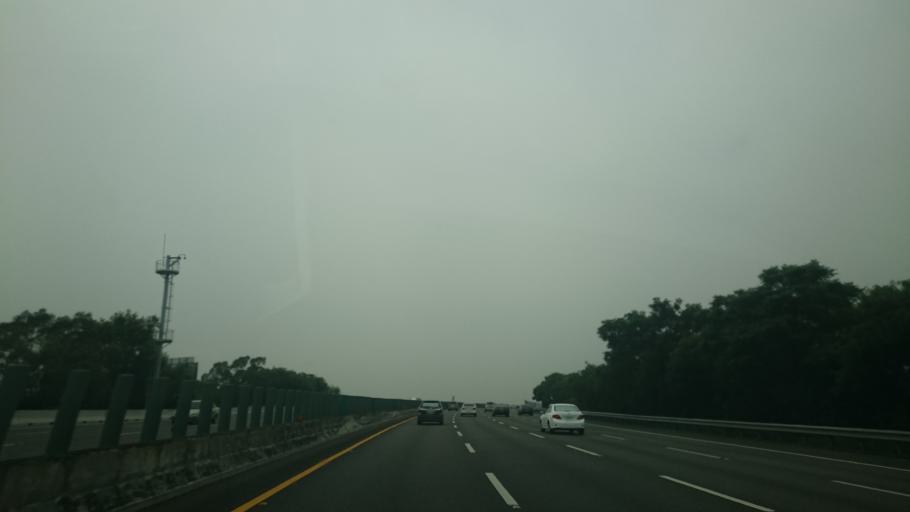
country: TW
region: Taiwan
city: Zhongxing New Village
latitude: 23.9672
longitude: 120.6488
